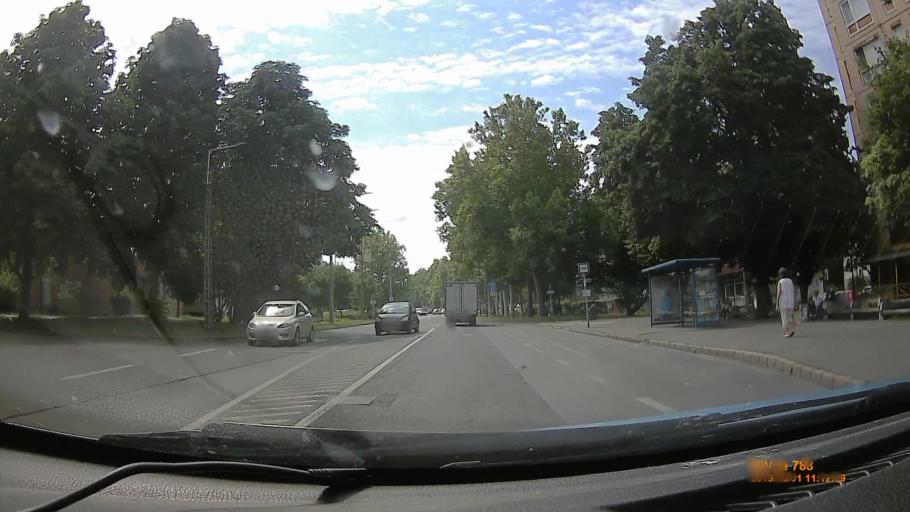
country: HU
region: Baranya
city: Pecs
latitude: 46.0443
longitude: 18.2153
